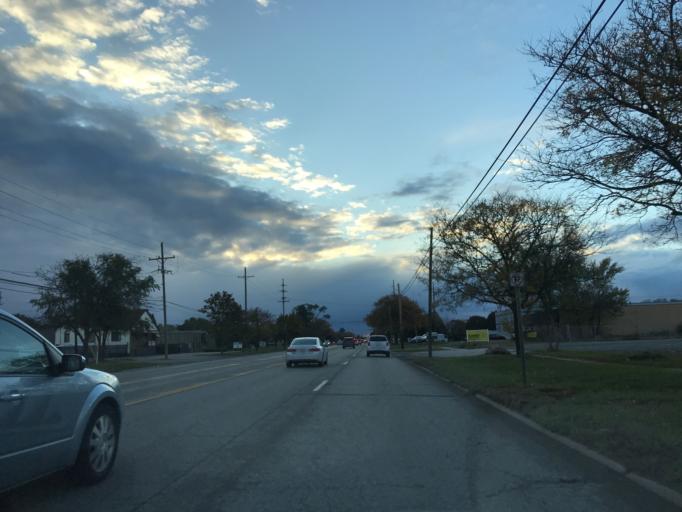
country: US
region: Michigan
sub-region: Oakland County
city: Farmington
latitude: 42.4413
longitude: -83.3500
